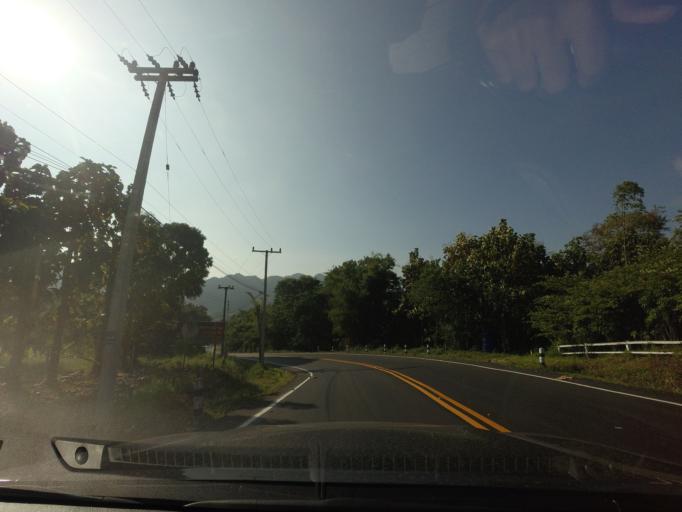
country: TH
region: Phetchabun
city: Lom Kao
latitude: 16.8735
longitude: 101.1319
